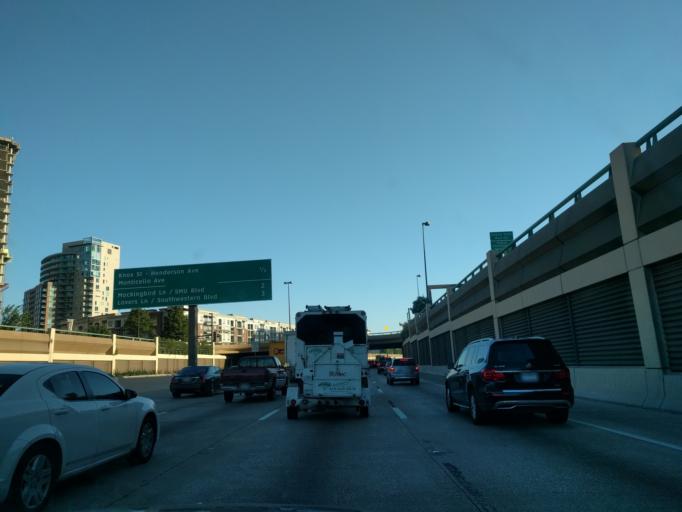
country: US
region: Texas
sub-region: Dallas County
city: Dallas
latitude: 32.8059
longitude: -96.7932
